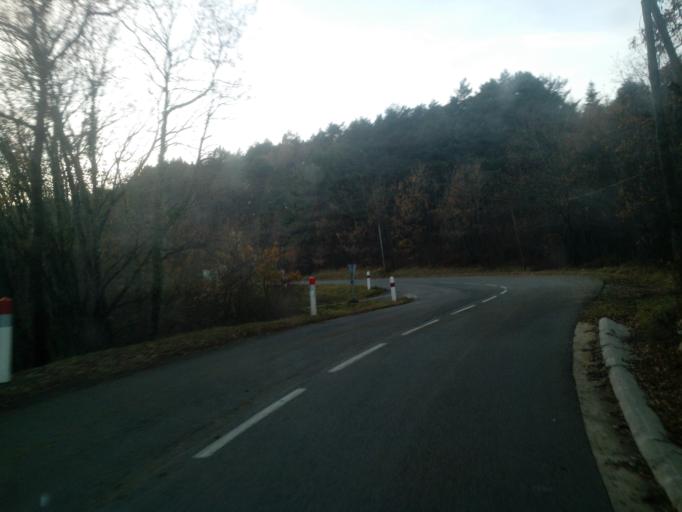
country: FR
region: Languedoc-Roussillon
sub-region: Departement de l'Aude
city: Chalabre
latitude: 42.9133
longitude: 2.0276
